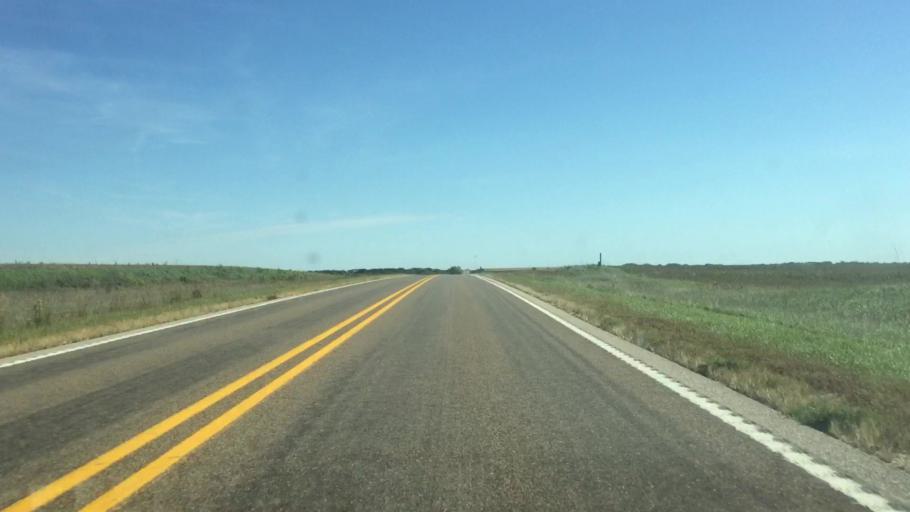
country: US
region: Nebraska
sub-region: Thayer County
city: Hebron
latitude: 40.1473
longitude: -97.5088
